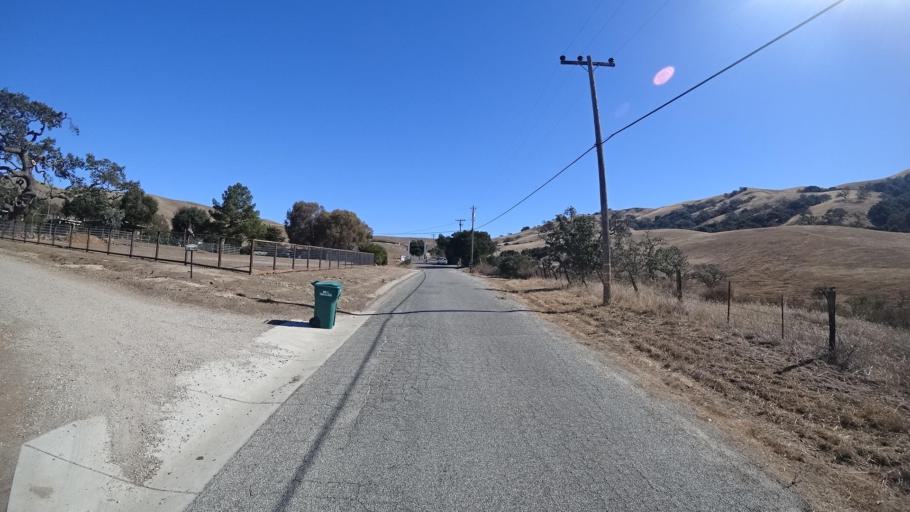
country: US
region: California
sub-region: Monterey County
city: Carmel Valley Village
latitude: 36.5419
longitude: -121.6527
